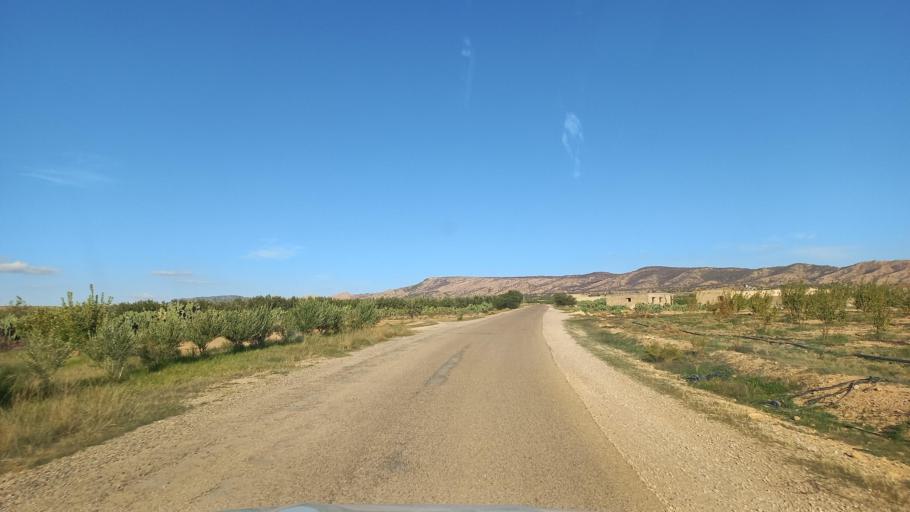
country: TN
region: Al Qasrayn
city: Sbiba
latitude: 35.3363
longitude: 9.1076
